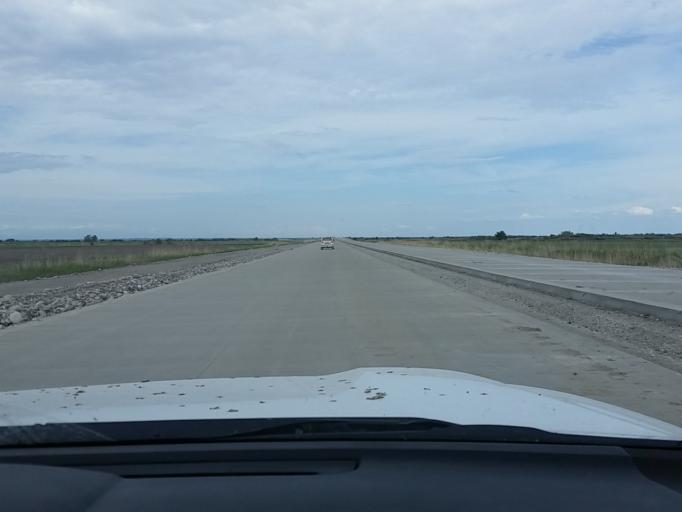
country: KZ
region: Almaty Oblysy
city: Zharkent
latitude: 44.0301
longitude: 79.9186
